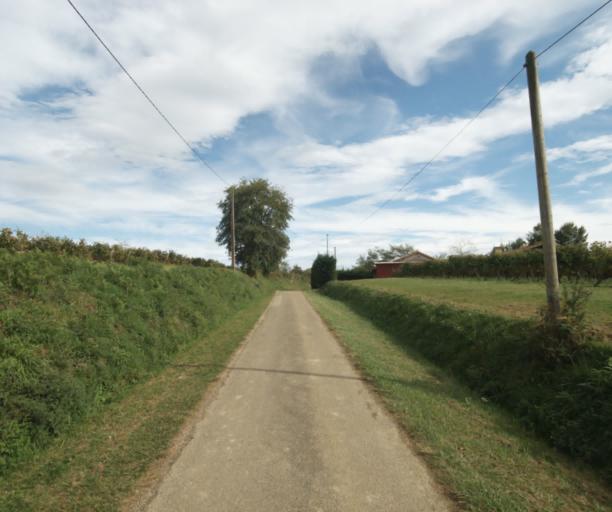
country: FR
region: Midi-Pyrenees
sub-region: Departement du Gers
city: Cazaubon
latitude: 43.8793
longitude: -0.1463
